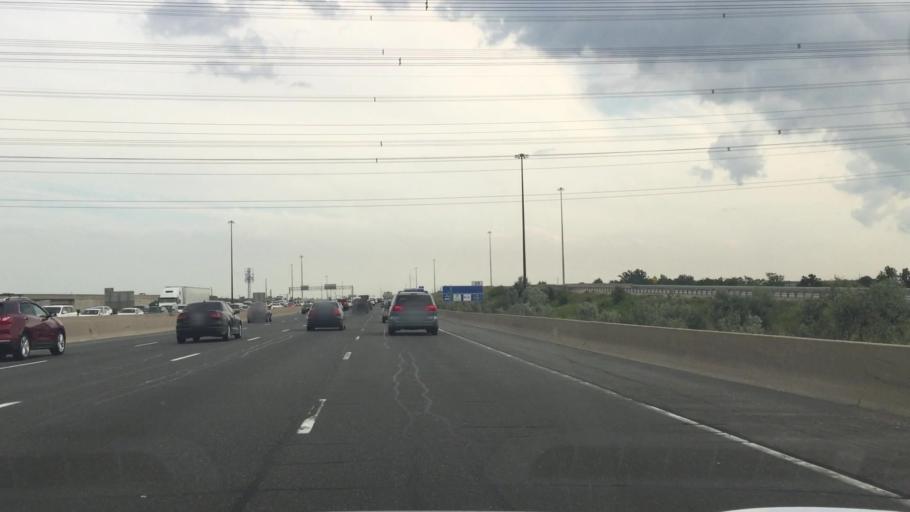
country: CA
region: Ontario
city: Concord
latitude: 43.7787
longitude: -79.5366
